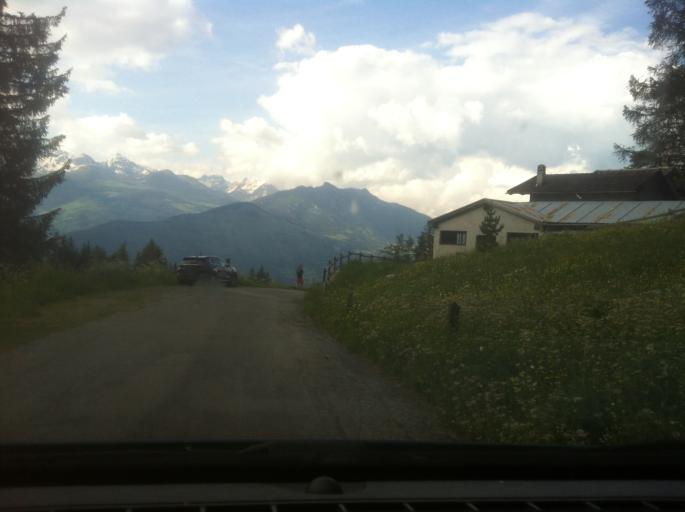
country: IT
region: Aosta Valley
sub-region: Valle d'Aosta
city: Nus
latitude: 45.7089
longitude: 7.4711
